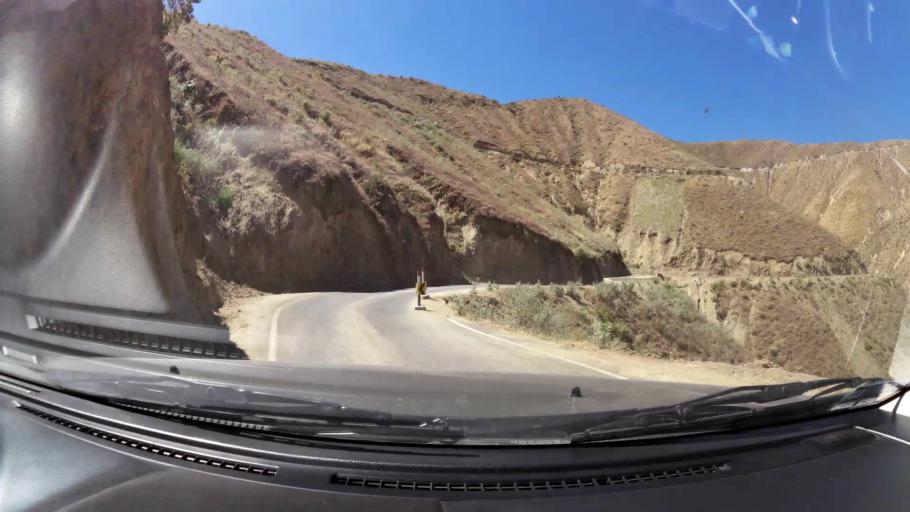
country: PE
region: Ica
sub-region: Provincia de Pisco
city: Huancano
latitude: -13.7246
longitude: -75.4581
